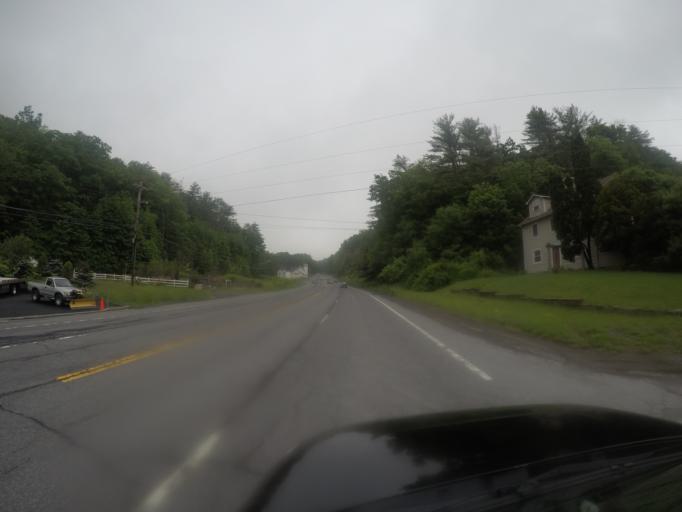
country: US
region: New York
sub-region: Ulster County
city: West Hurley
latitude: 41.9693
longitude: -74.0707
